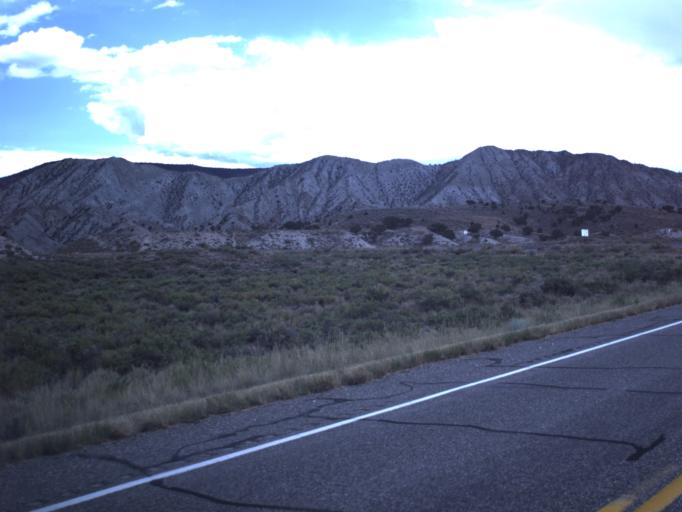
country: US
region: Utah
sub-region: Sevier County
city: Aurora
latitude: 38.8225
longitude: -111.9417
